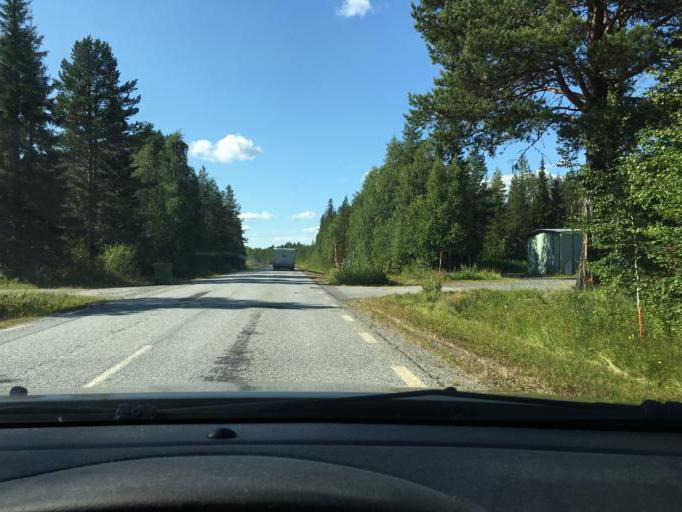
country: SE
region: Norrbotten
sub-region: Lulea Kommun
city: Ranea
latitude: 66.0464
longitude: 22.2817
